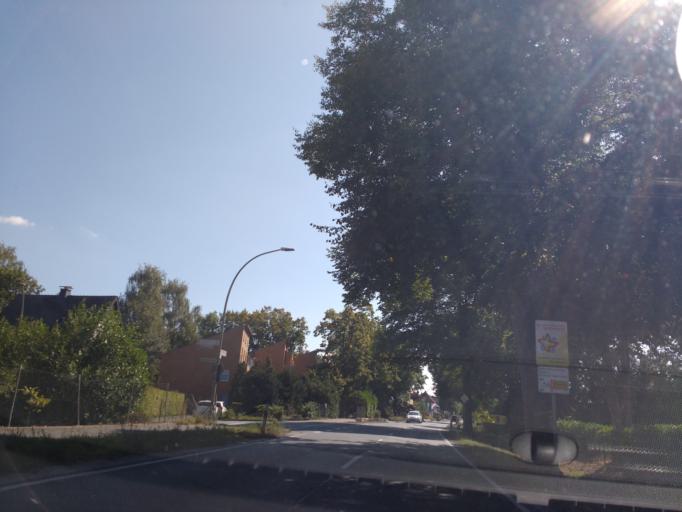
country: DE
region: North Rhine-Westphalia
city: Rietberg
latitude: 51.8139
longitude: 8.4218
